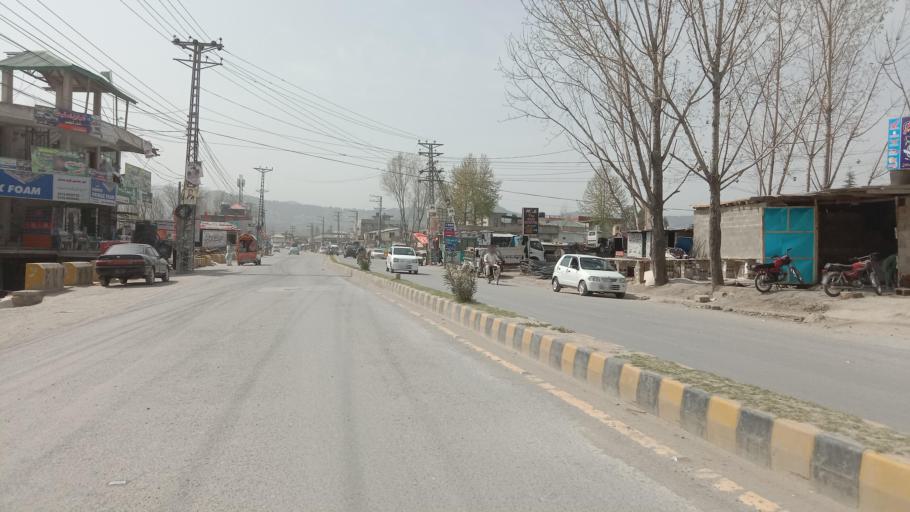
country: PK
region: Khyber Pakhtunkhwa
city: Abbottabad
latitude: 34.1579
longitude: 73.2499
